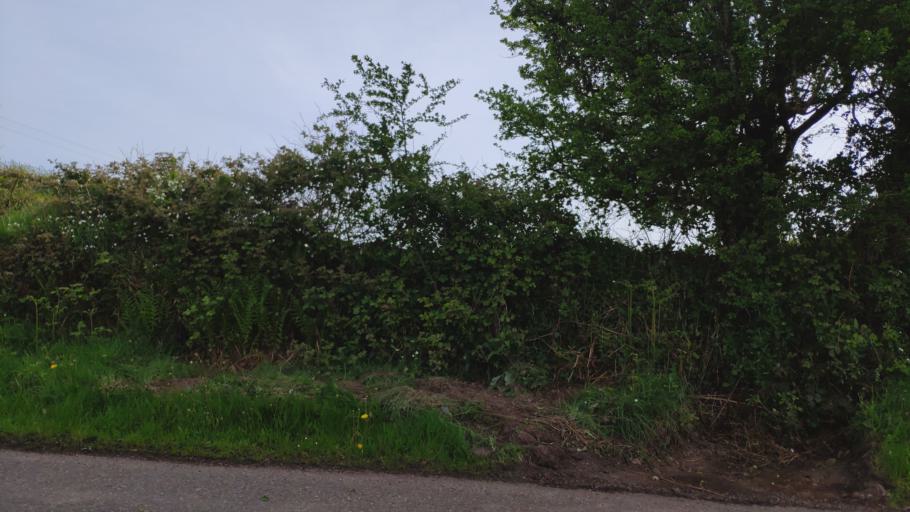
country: IE
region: Munster
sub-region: County Cork
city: Blarney
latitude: 51.9598
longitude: -8.5122
